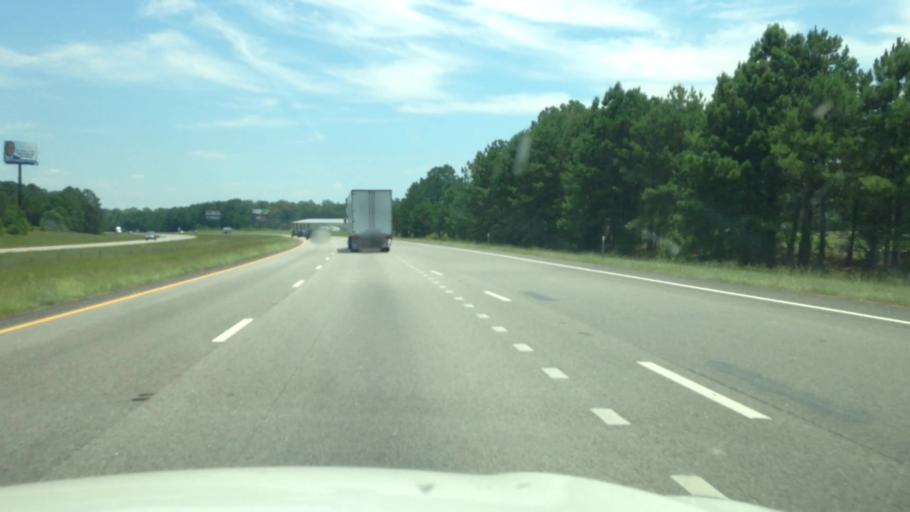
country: US
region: South Carolina
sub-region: Florence County
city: Timmonsville
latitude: 34.2027
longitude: -79.9083
